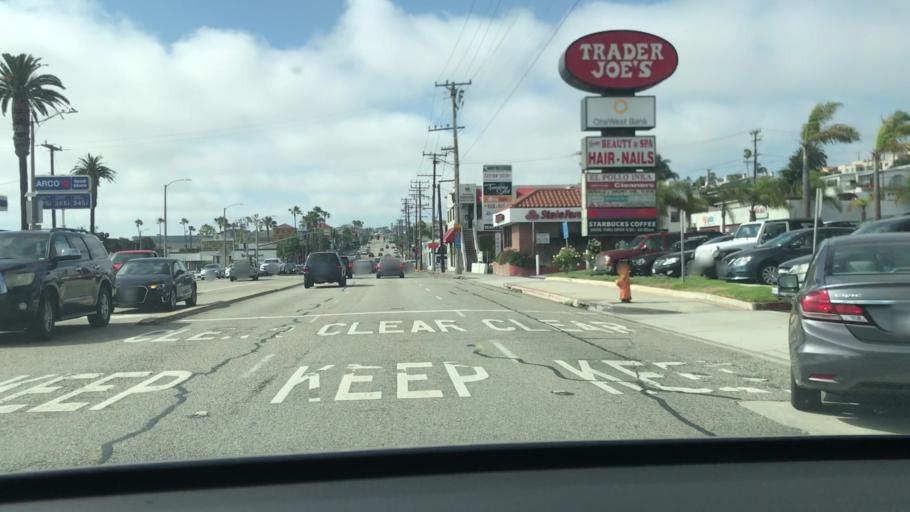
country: US
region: California
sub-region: Los Angeles County
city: Hermosa Beach
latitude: 33.8634
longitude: -118.3926
